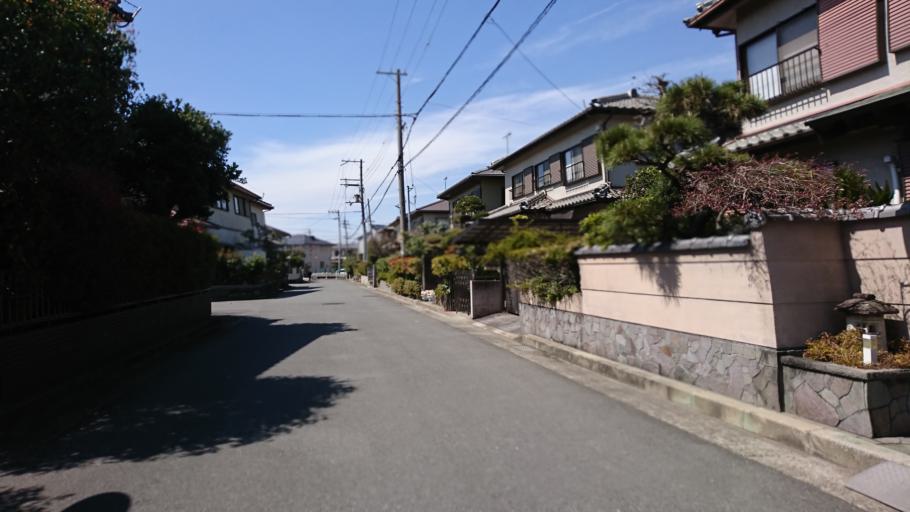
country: JP
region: Hyogo
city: Kakogawacho-honmachi
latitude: 34.7516
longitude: 134.8776
